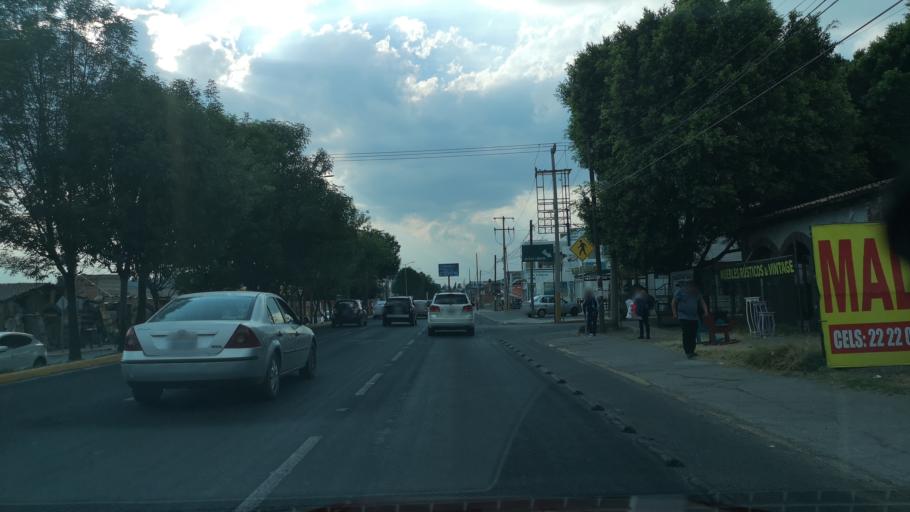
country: MX
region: Puebla
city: Cholula
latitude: 19.0701
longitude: -98.3121
